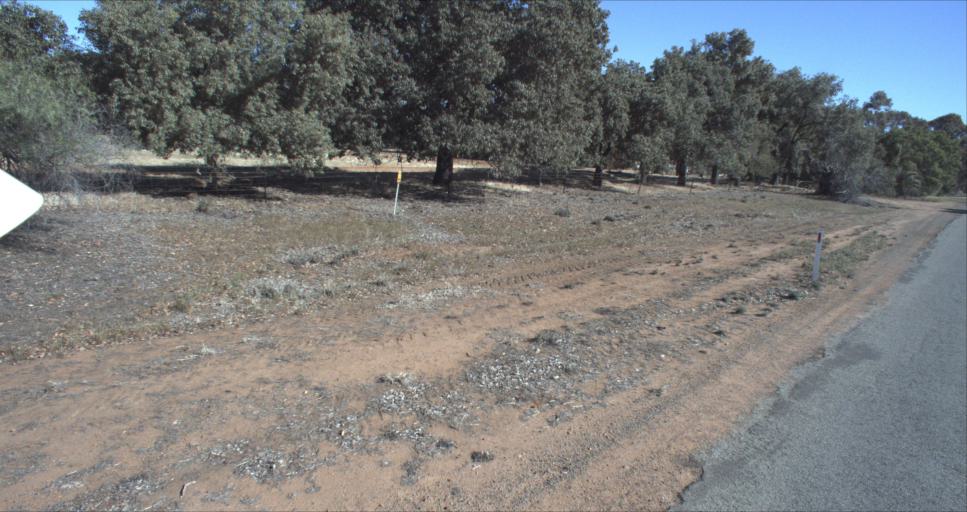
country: AU
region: New South Wales
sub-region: Leeton
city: Leeton
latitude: -34.5761
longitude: 146.3097
